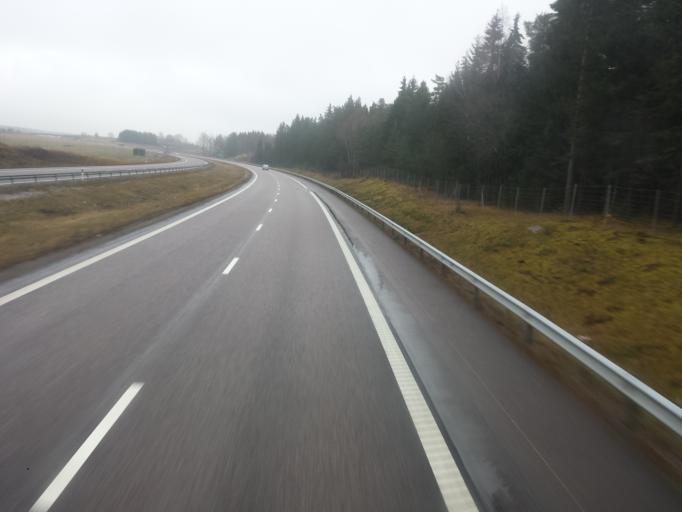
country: SE
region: Soedermanland
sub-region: Nykopings Kommun
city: Stigtomta
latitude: 58.7528
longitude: 16.7442
